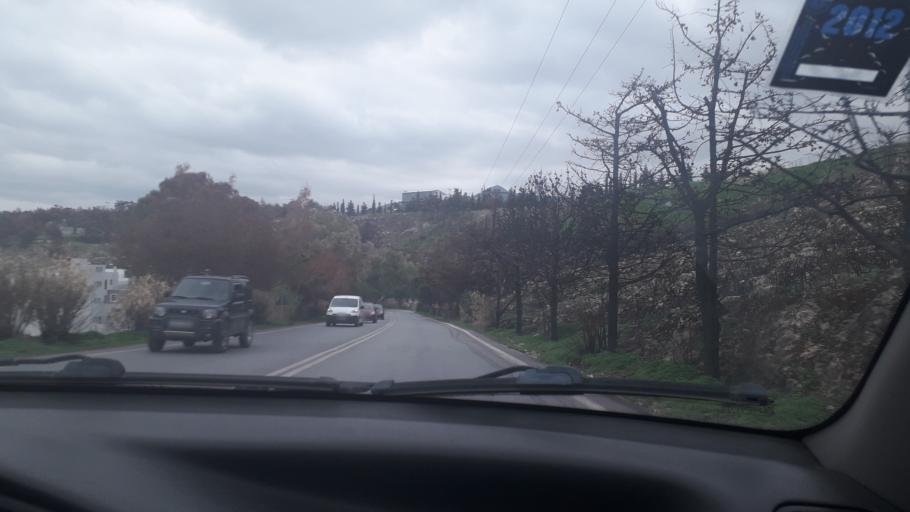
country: GR
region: Crete
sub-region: Nomos Rethymnis
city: Rethymno
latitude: 35.3580
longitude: 24.4701
